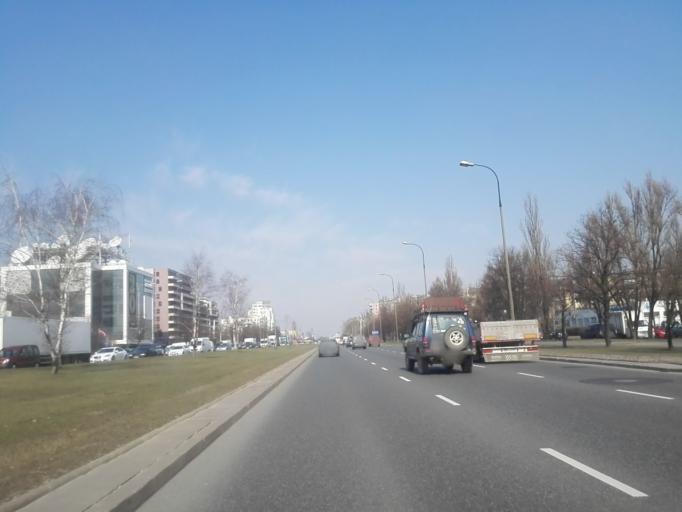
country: PL
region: Masovian Voivodeship
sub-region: Warszawa
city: Mokotow
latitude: 52.1795
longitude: 21.0451
